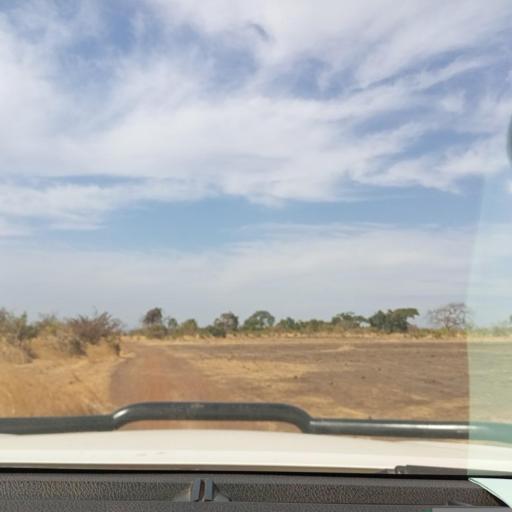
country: ML
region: Koulikoro
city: Kati
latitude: 12.7435
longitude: -8.2488
